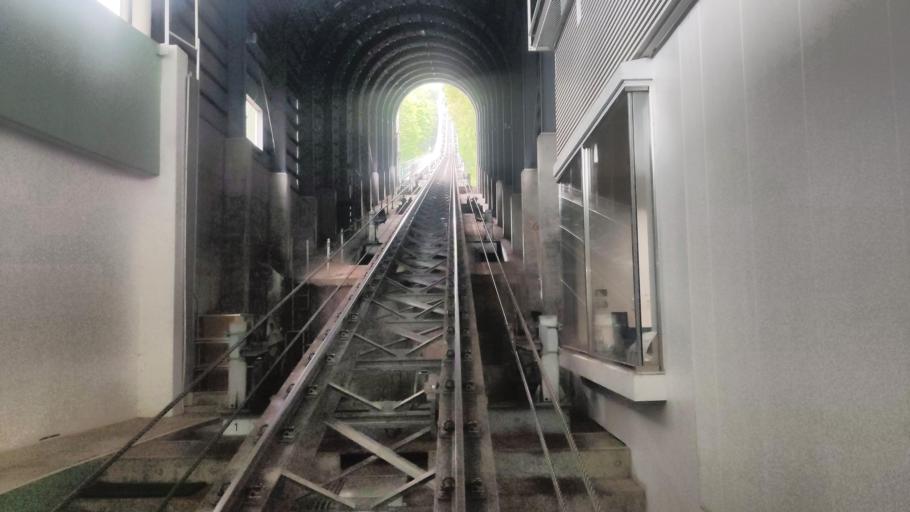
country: JP
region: Hokkaido
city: Sapporo
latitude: 43.0222
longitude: 141.3250
